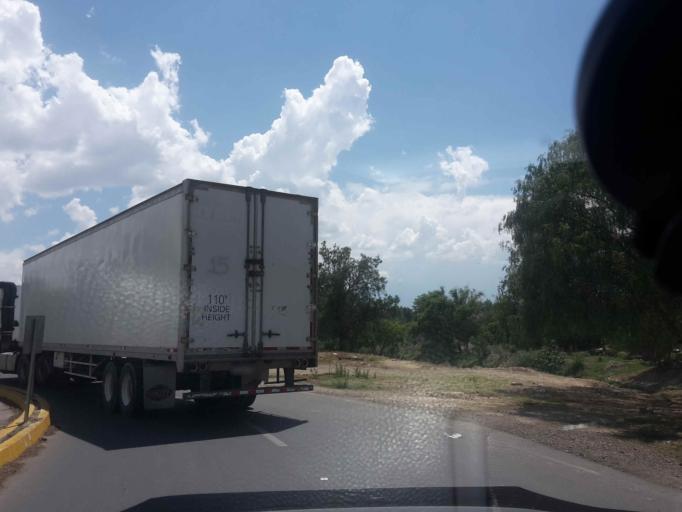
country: BO
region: Cochabamba
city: Cochabamba
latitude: -17.4104
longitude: -66.1751
